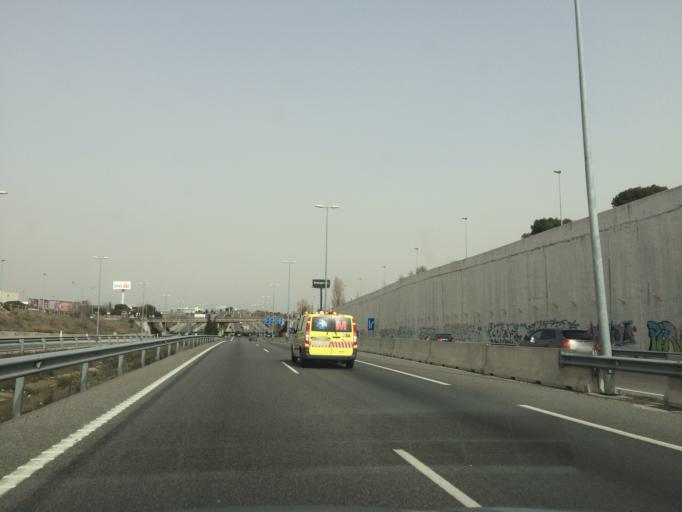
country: ES
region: Madrid
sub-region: Provincia de Madrid
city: Las Rozas de Madrid
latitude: 40.5154
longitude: -3.8934
